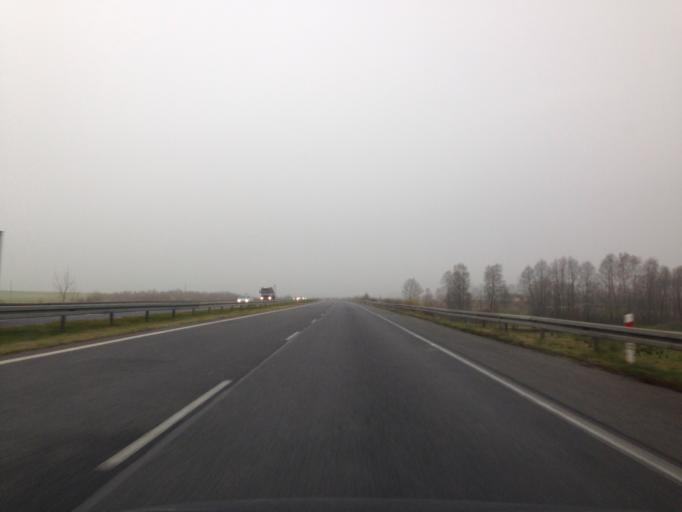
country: PL
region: Lodz Voivodeship
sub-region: Powiat piotrkowski
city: Wola Krzysztoporska
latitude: 51.2828
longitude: 19.5364
